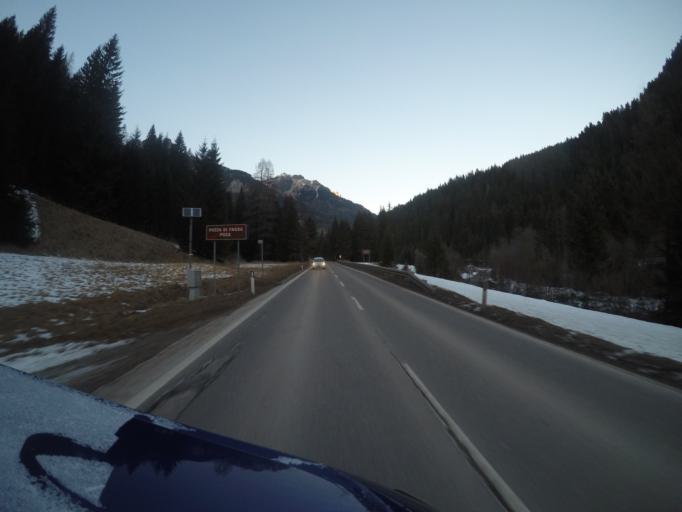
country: IT
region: Trentino-Alto Adige
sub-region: Provincia di Trento
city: Mazzin
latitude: 46.4507
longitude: 11.6980
